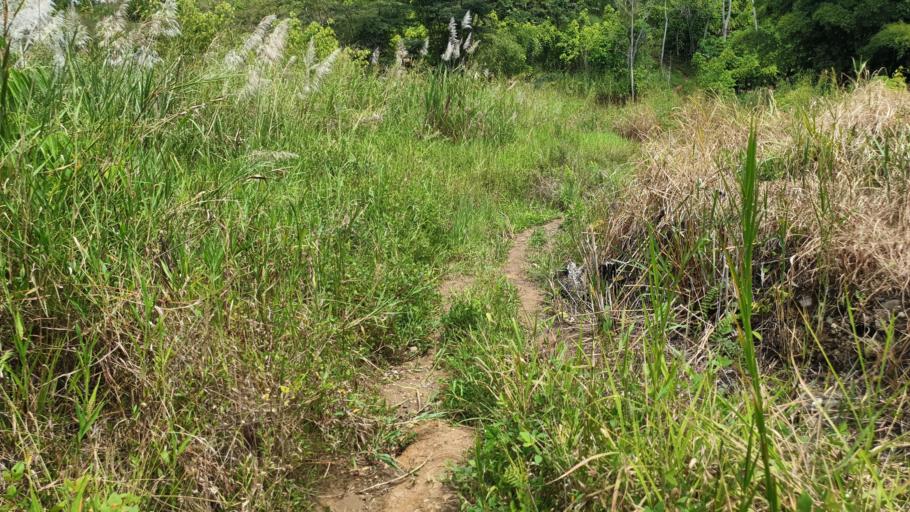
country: PG
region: Jiwaka
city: Minj
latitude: -5.9135
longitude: 144.8280
